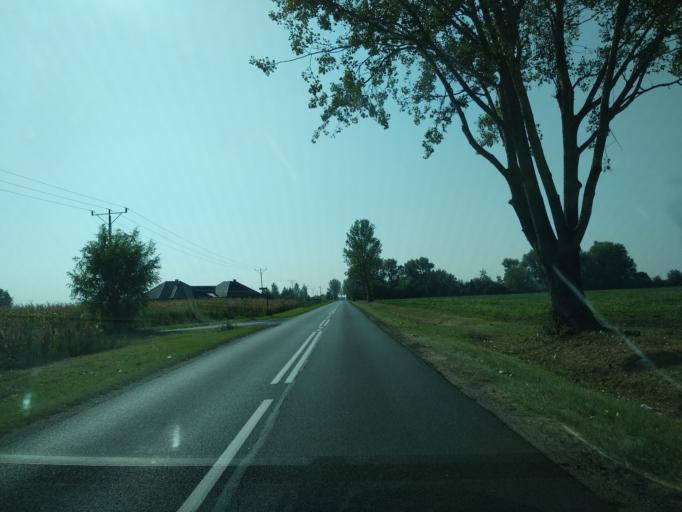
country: PL
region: Lower Silesian Voivodeship
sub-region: Powiat wroclawski
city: Zerniki Wroclawskie
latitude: 51.0293
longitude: 17.0330
